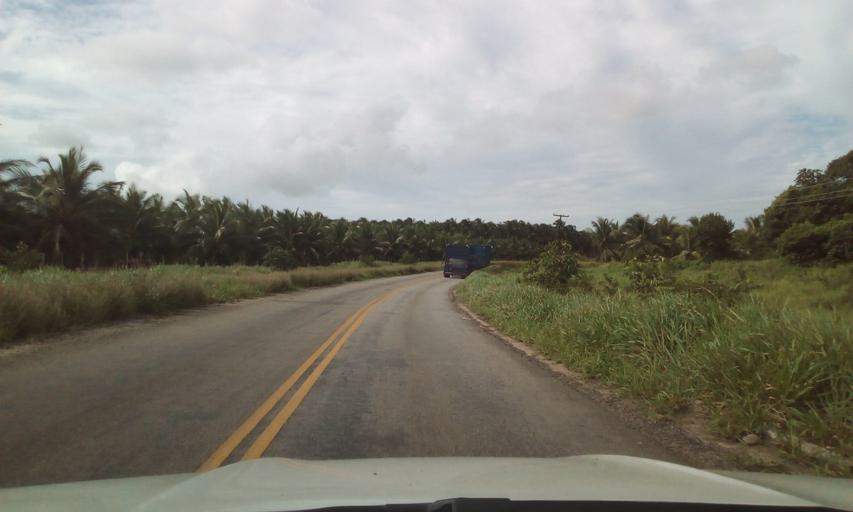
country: BR
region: Paraiba
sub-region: Cabedelo
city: Cabedelo
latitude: -6.9405
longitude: -34.9070
